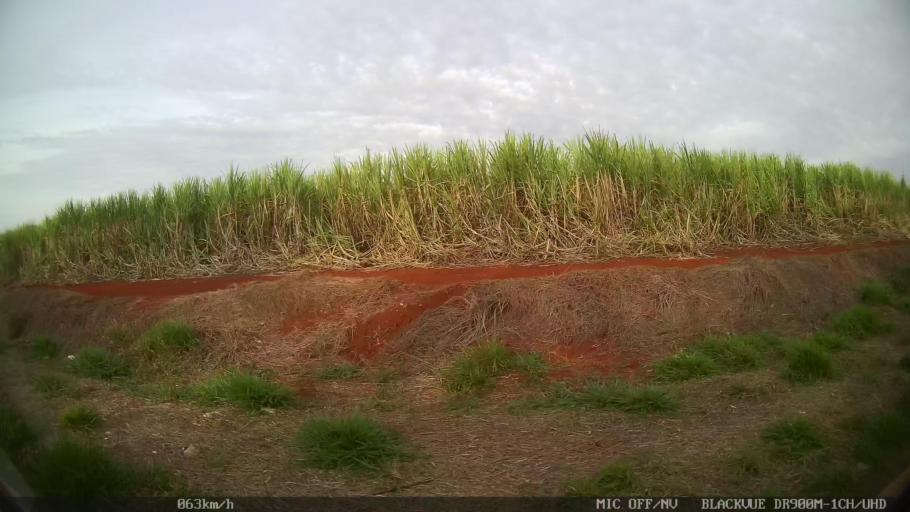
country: BR
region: Sao Paulo
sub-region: Piracicaba
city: Piracicaba
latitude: -22.7155
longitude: -47.5815
